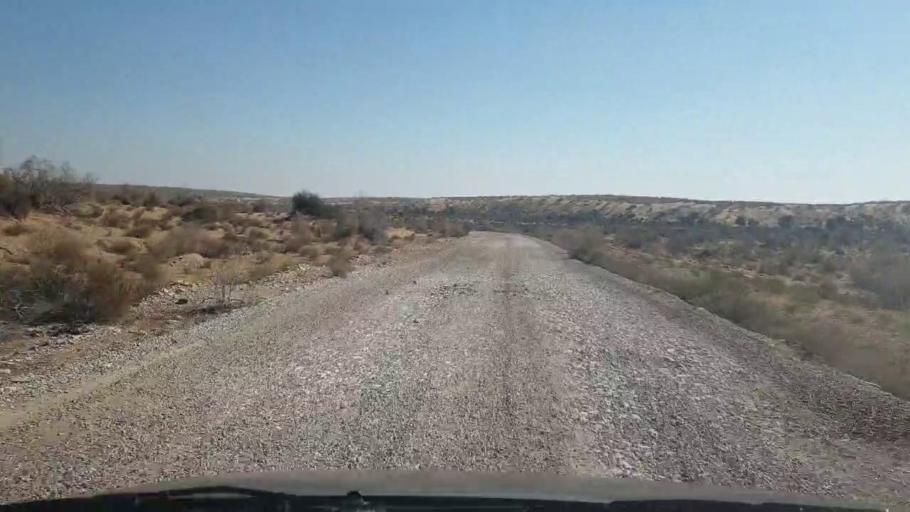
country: PK
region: Sindh
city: Bozdar
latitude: 27.0226
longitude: 68.7161
